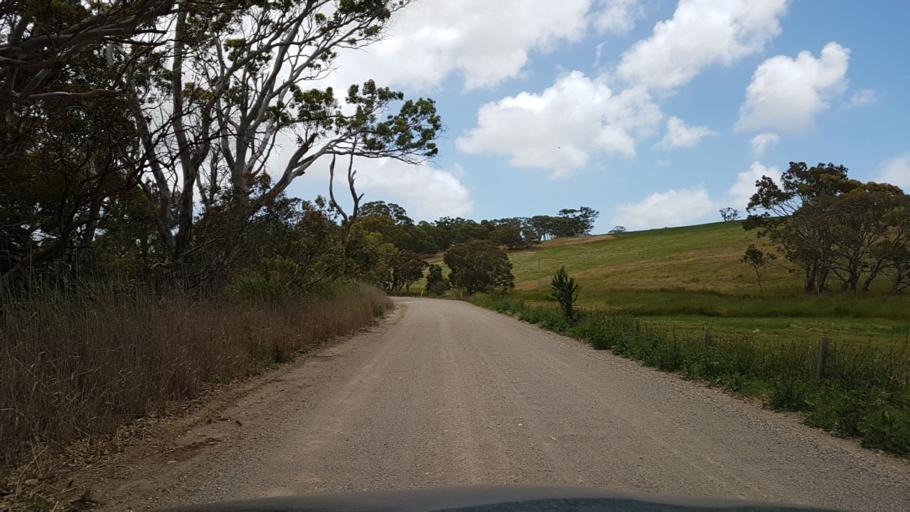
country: AU
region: South Australia
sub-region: Onkaparinga
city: Aldinga
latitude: -35.3725
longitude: 138.5158
